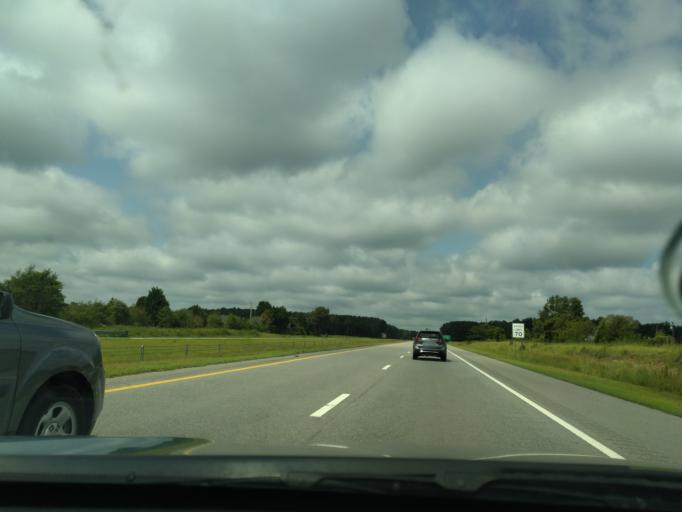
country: US
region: North Carolina
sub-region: Martin County
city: Williamston
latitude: 35.8181
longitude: -77.0809
